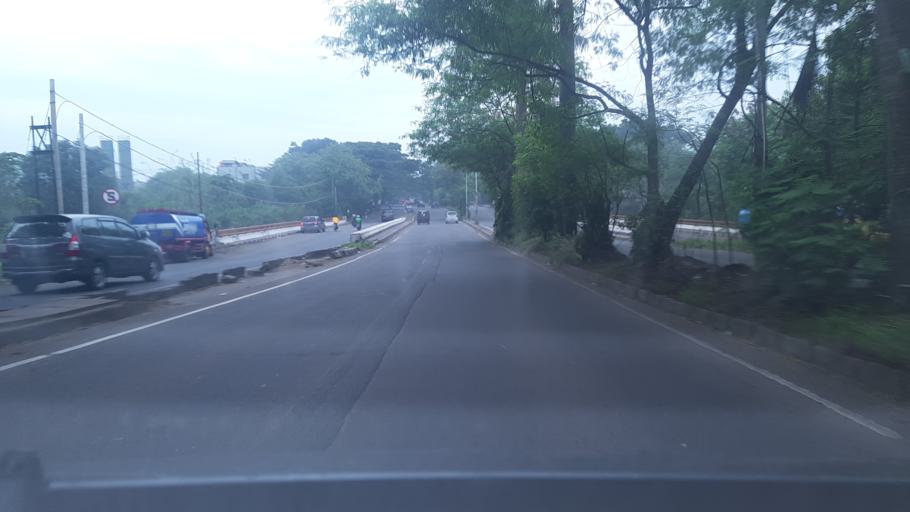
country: ID
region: West Java
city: Cibinong
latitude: -6.5214
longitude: 106.8401
